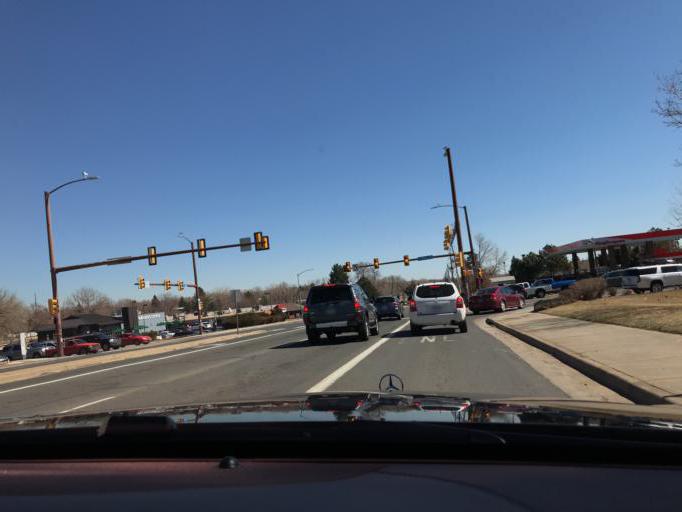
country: US
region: Colorado
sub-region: Jefferson County
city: Arvada
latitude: 39.8126
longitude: -105.1387
